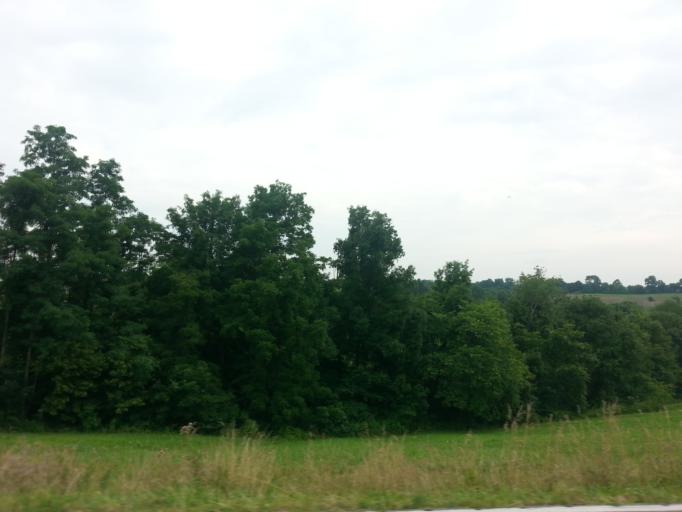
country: US
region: Kentucky
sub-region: Robertson County
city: Mount Olivet
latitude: 38.5305
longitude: -84.0128
